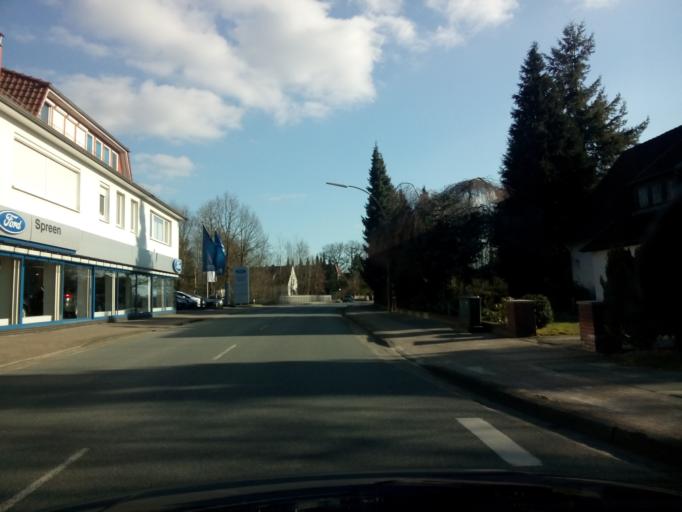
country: DE
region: Lower Saxony
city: Osterholz-Scharmbeck
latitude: 53.2390
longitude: 8.7827
